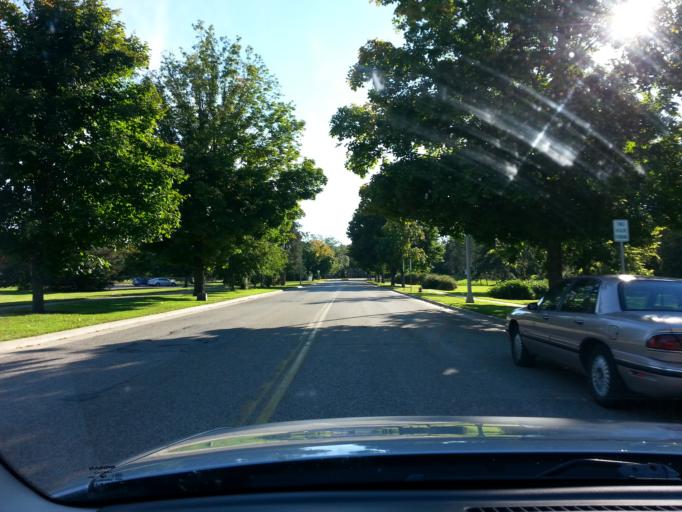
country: US
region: Minnesota
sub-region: Olmsted County
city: Rochester
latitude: 44.0145
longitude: -92.4691
